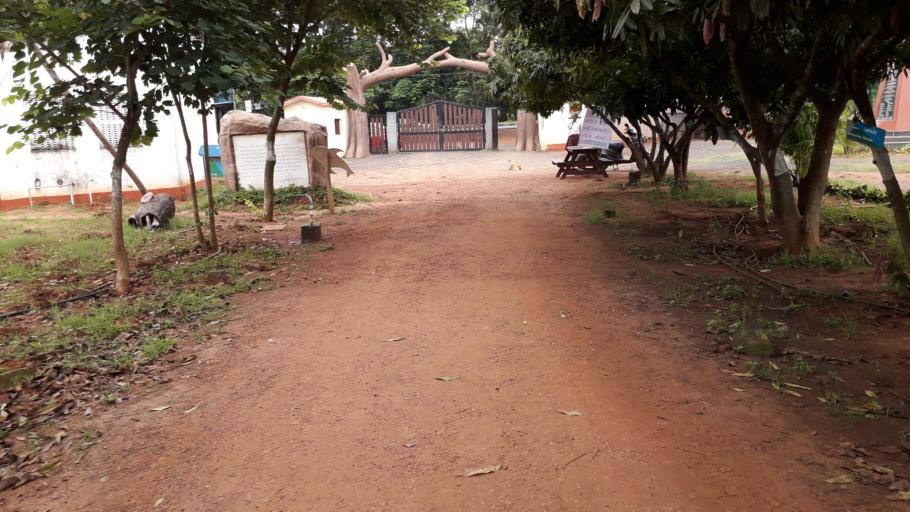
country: IN
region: Andhra Pradesh
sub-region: East Godavari
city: Rajahmundry
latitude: 17.0347
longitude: 81.8262
